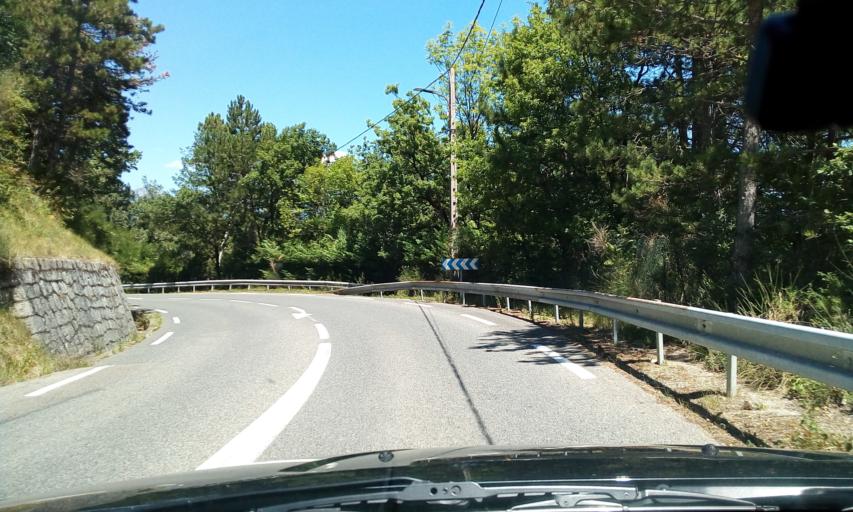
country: FR
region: Rhone-Alpes
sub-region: Departement de l'Isere
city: Seyssins
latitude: 45.1633
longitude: 5.6824
